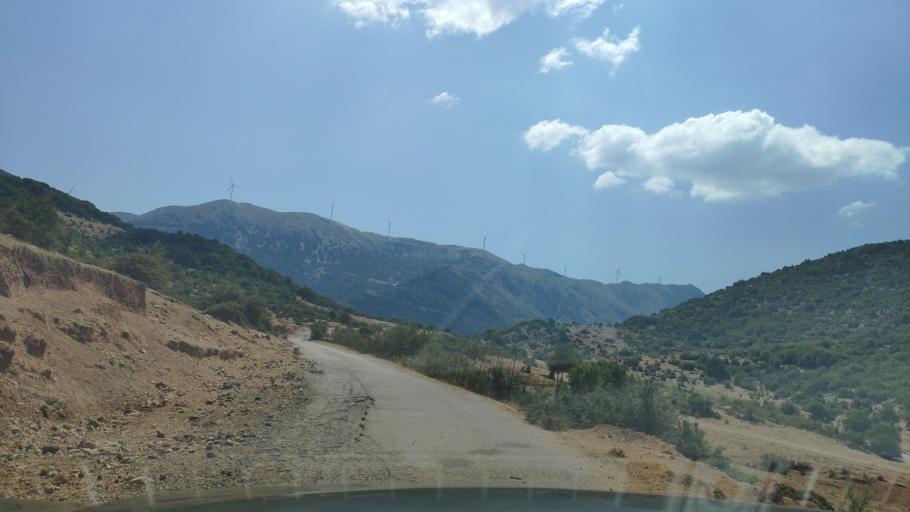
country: GR
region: West Greece
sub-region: Nomos Aitolias kai Akarnanias
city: Monastirakion
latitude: 38.7976
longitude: 20.9531
